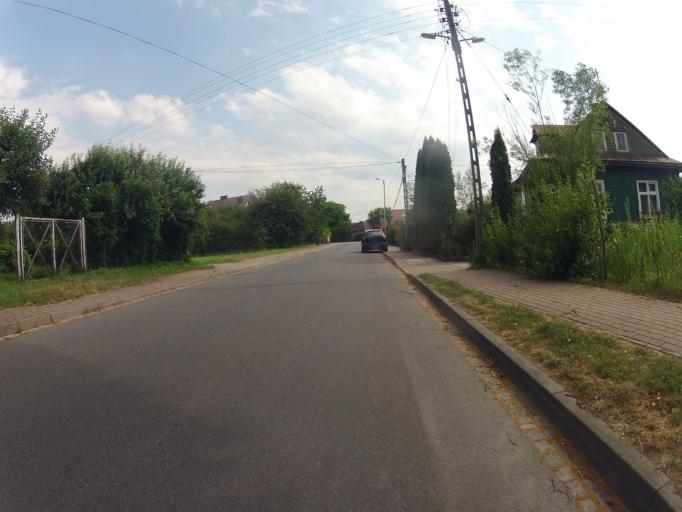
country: PL
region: Lesser Poland Voivodeship
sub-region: Powiat nowosadecki
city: Stary Sacz
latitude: 49.5596
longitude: 20.6403
